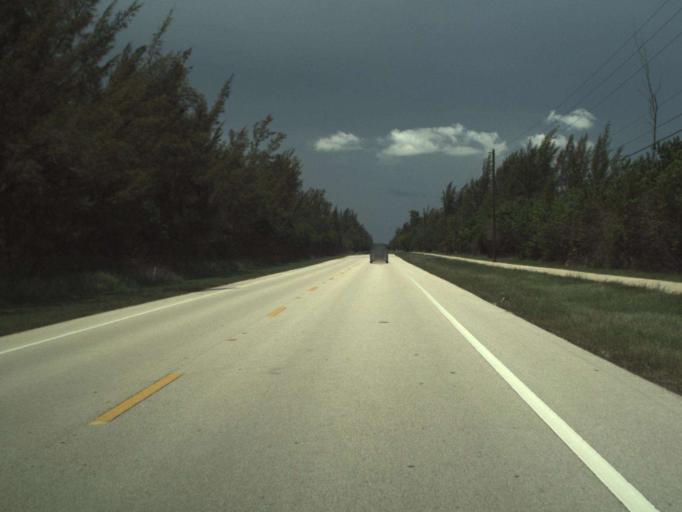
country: US
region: Florida
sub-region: Saint Lucie County
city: Indian River Estates
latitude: 27.3991
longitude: -80.2657
